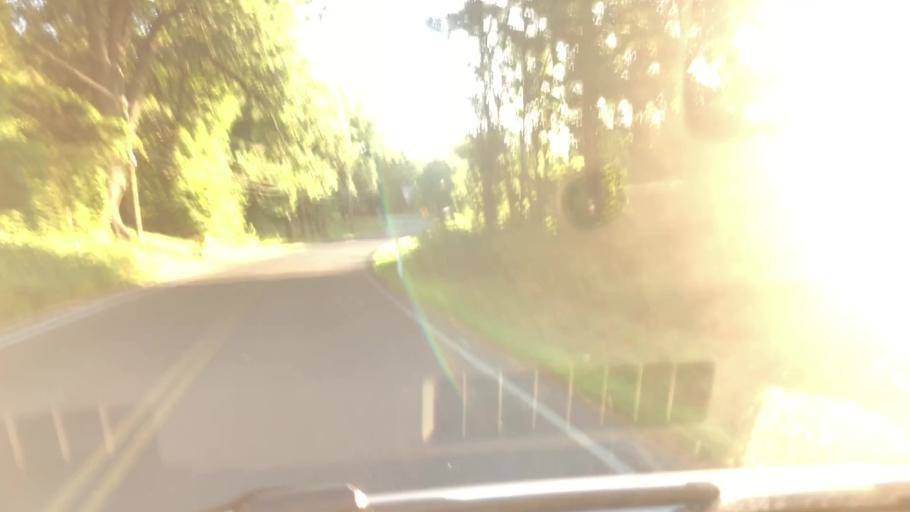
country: US
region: Massachusetts
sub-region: Hampshire County
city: Southampton
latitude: 42.2730
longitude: -72.7168
